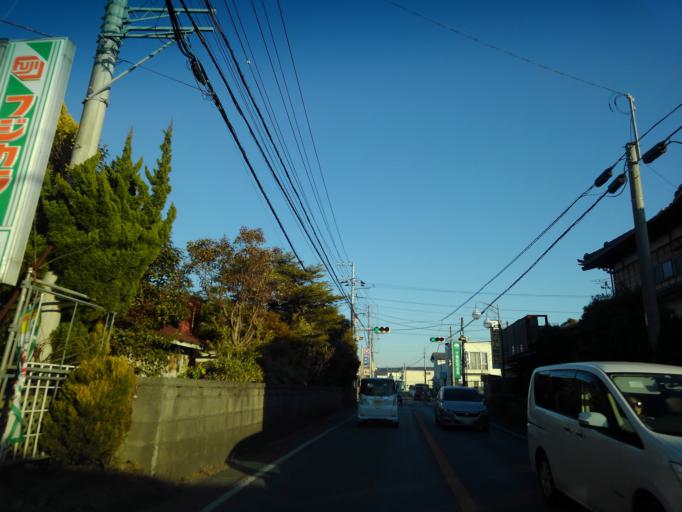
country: JP
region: Chiba
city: Kimitsu
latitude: 35.3062
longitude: 139.9547
